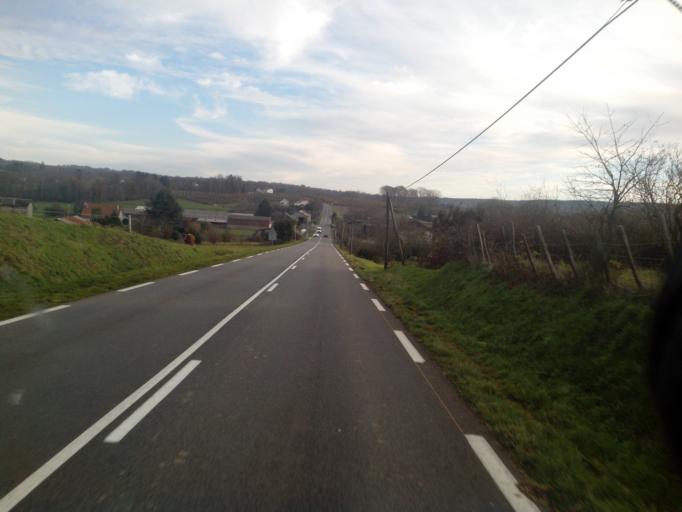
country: FR
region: Limousin
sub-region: Departement de la Haute-Vienne
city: Neuvic-Entier
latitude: 45.7371
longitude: 1.6111
